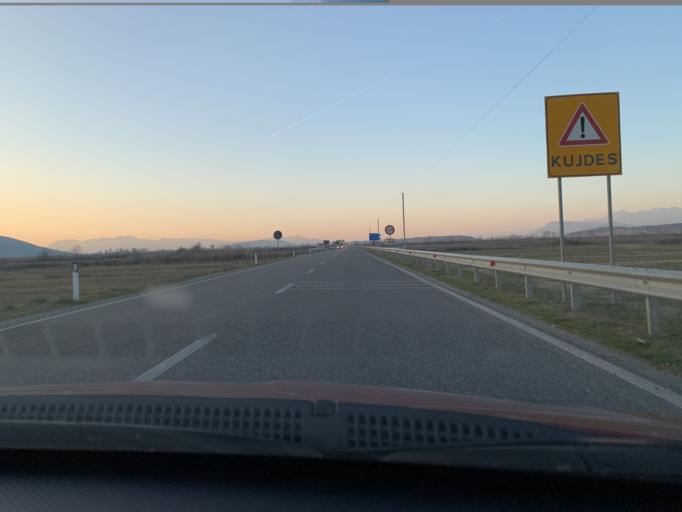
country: AL
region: Lezhe
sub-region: Rrethi i Lezhes
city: Balldreni i Ri
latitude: 41.8708
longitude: 19.6324
